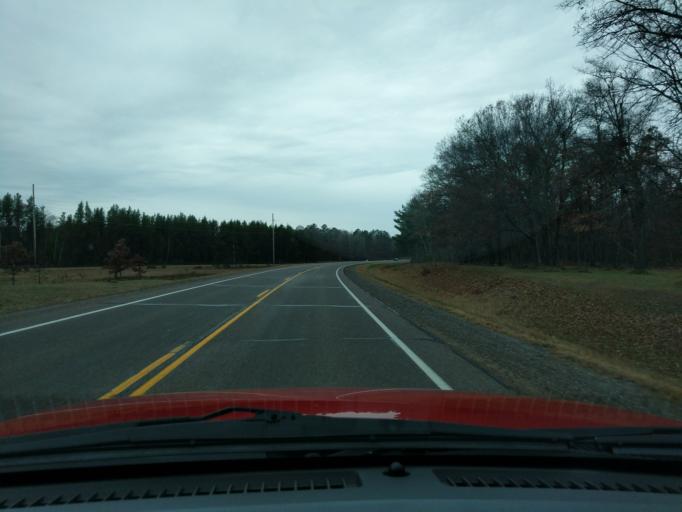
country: US
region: Wisconsin
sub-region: Washburn County
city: Spooner
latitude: 45.8160
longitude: -91.9672
